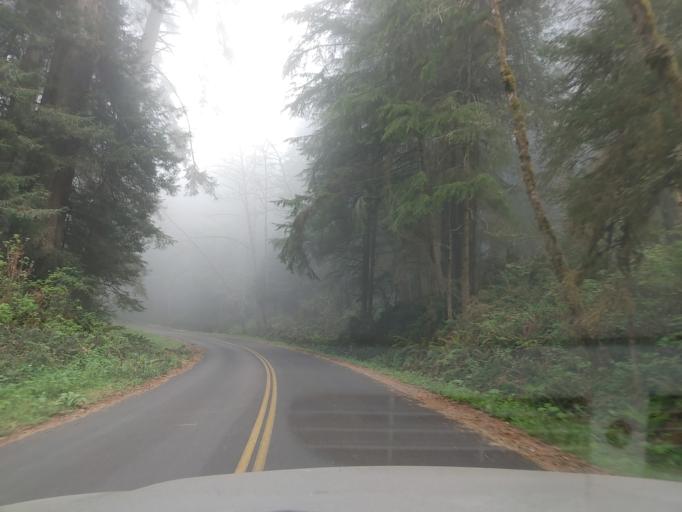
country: US
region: California
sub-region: Del Norte County
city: Bertsch-Oceanview
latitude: 41.4651
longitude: -124.0551
